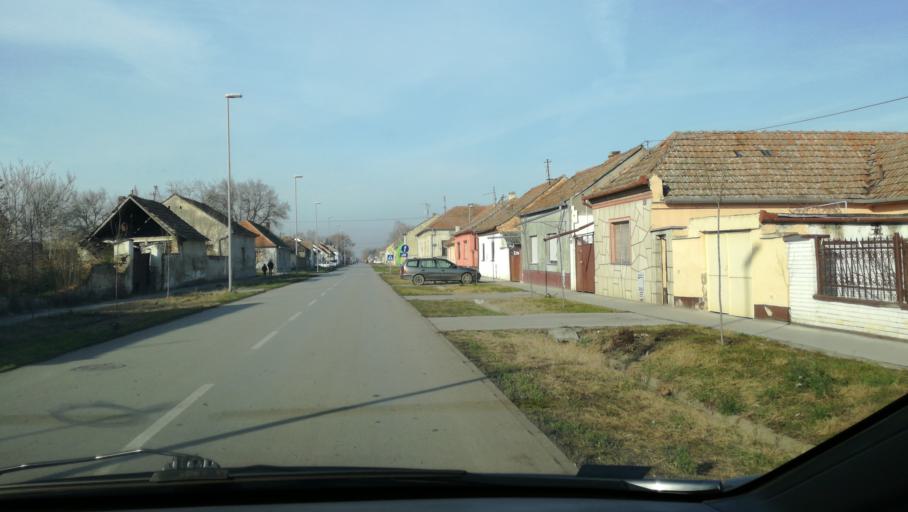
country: RS
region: Autonomna Pokrajina Vojvodina
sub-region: Severnobanatski Okrug
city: Kikinda
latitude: 45.8301
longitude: 20.4846
